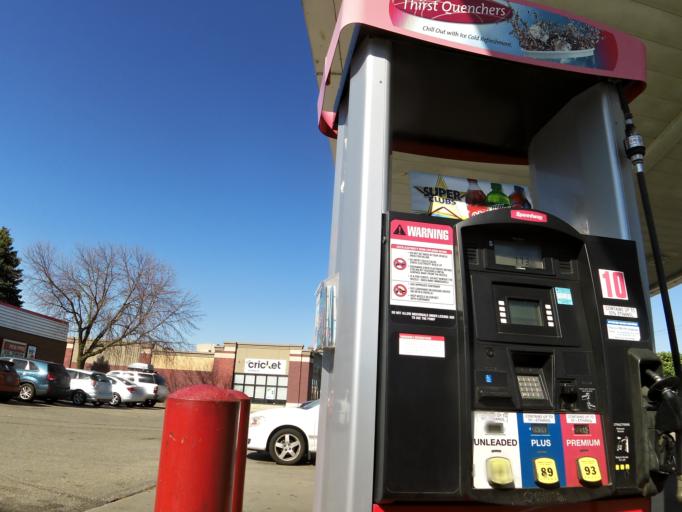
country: US
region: Wisconsin
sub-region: Rock County
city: Beloit
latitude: 42.5243
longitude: -88.9853
